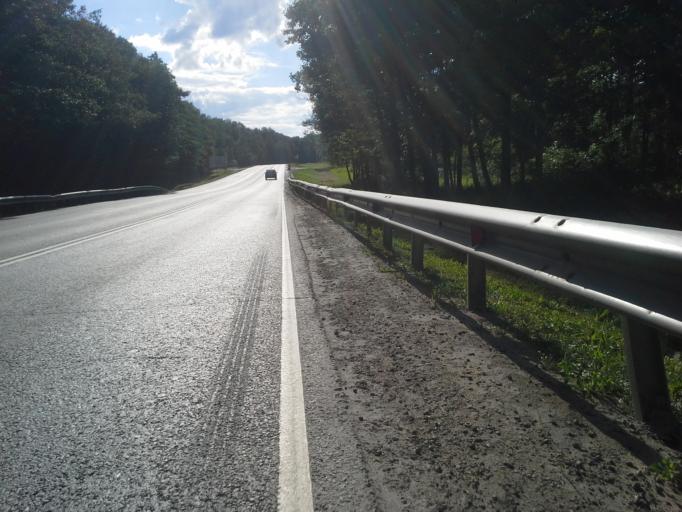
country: RU
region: Moskovskaya
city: L'vovskiy
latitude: 55.3341
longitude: 37.4843
